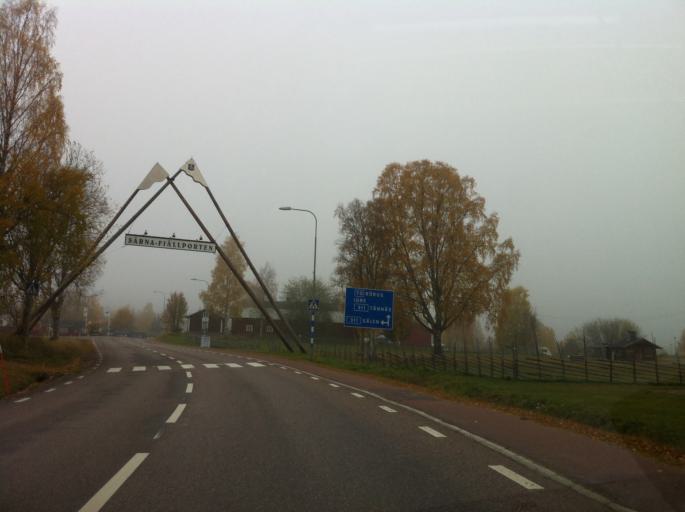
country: NO
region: Hedmark
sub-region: Trysil
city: Innbygda
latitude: 61.6924
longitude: 13.1469
